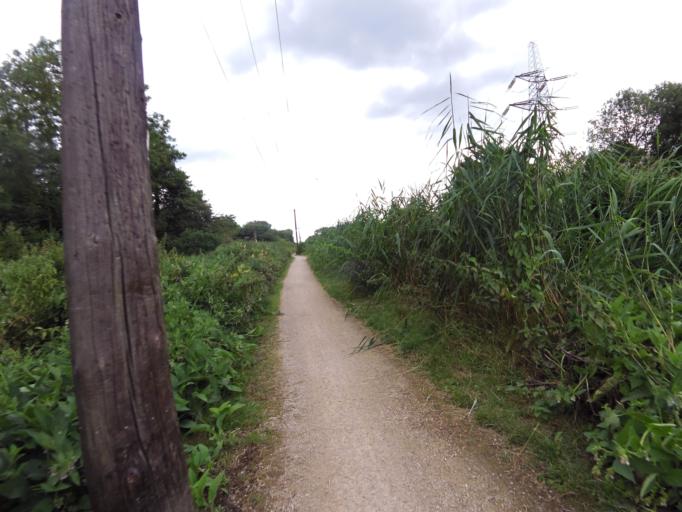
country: GB
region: England
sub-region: Hertfordshire
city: Cheshunt
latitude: 51.7192
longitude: -0.0148
